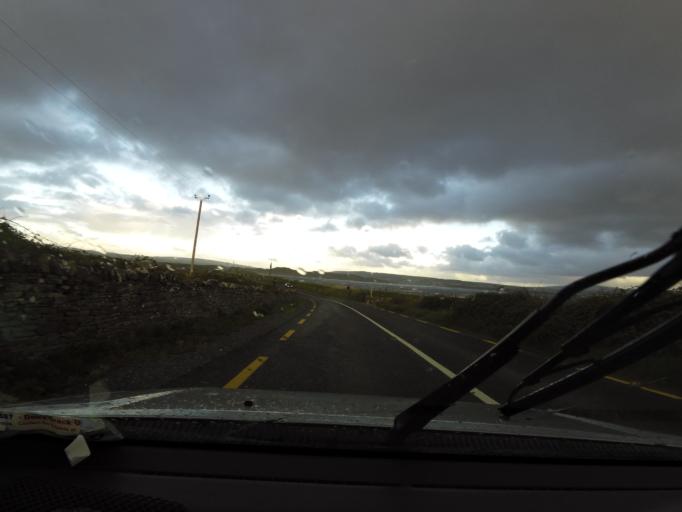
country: IE
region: Munster
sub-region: An Clar
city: Kilrush
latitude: 52.9442
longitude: -9.3731
